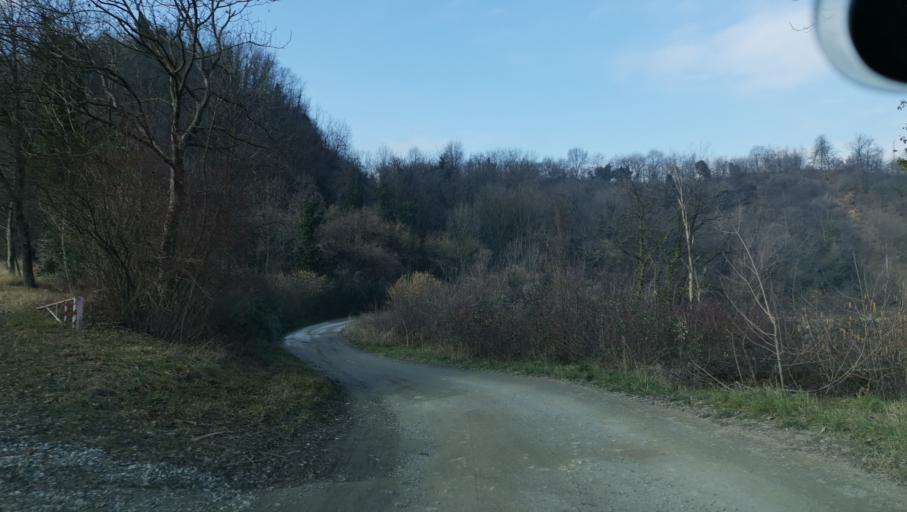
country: IT
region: Piedmont
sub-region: Provincia di Torino
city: Gassino Torinese
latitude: 45.1074
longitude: 7.8405
